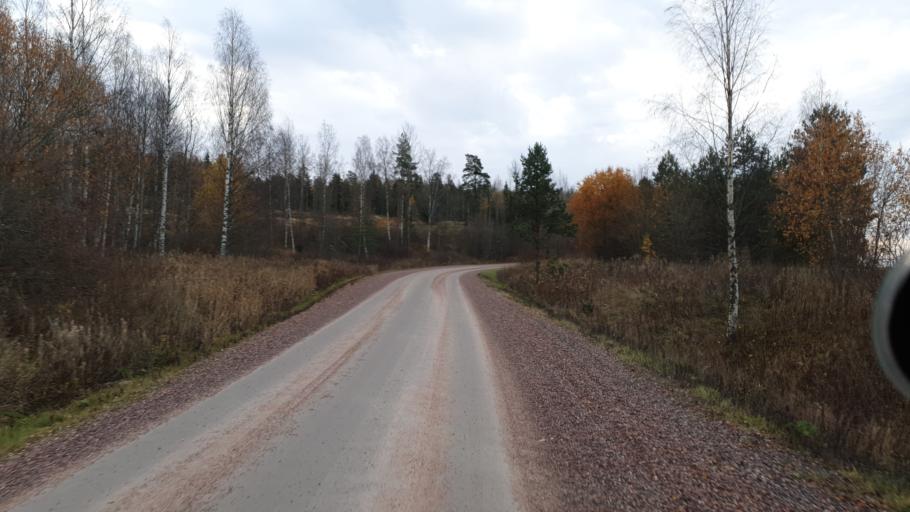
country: FI
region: Uusimaa
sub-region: Helsinki
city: Siuntio
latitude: 60.1357
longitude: 24.2746
